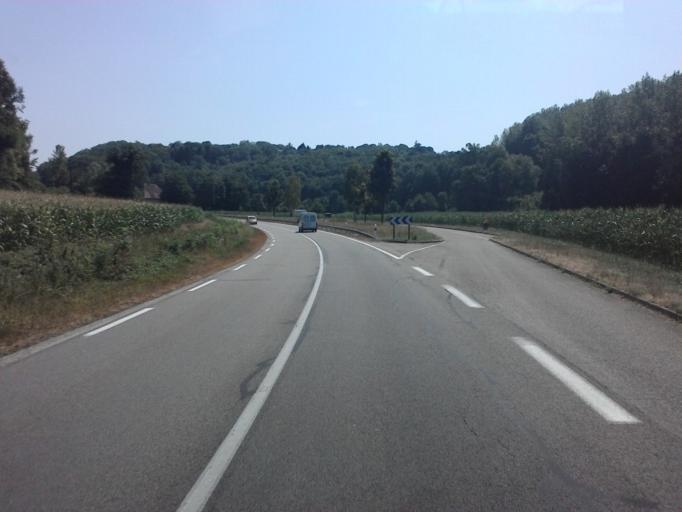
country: FR
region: Rhone-Alpes
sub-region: Departement de l'Isere
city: Corbelin
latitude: 45.5997
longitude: 5.5339
